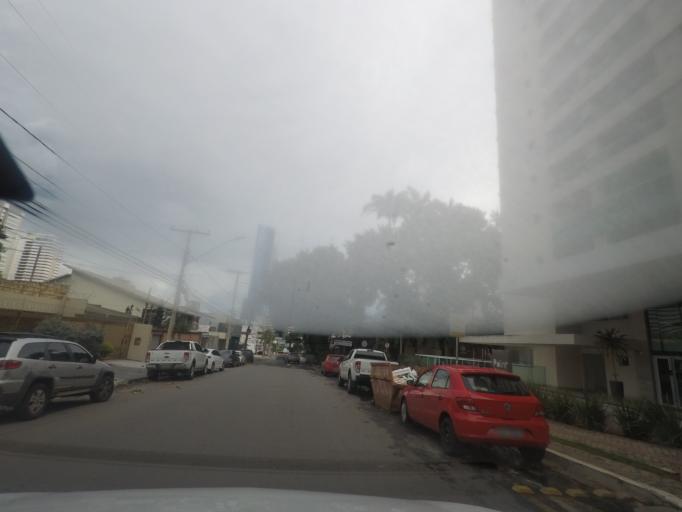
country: BR
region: Goias
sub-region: Goiania
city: Goiania
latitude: -16.6997
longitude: -49.2670
